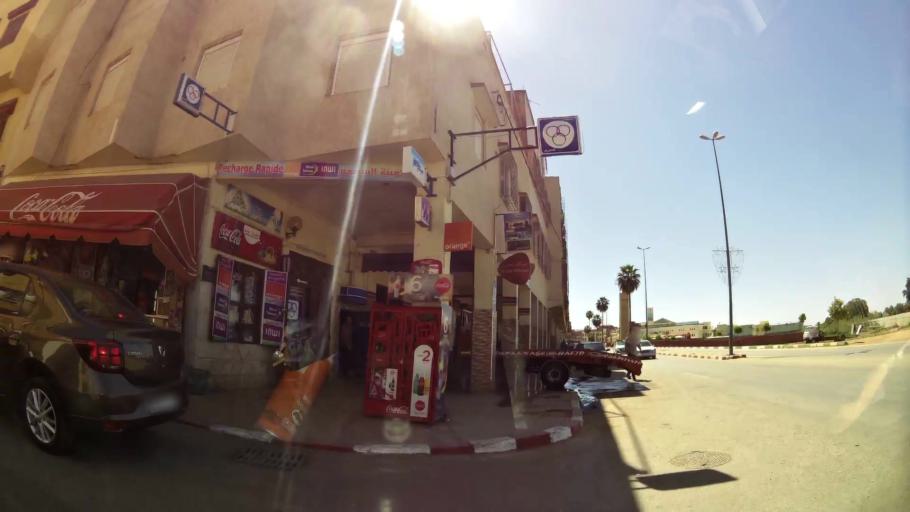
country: MA
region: Meknes-Tafilalet
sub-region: Meknes
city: Meknes
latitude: 33.8698
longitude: -5.5521
